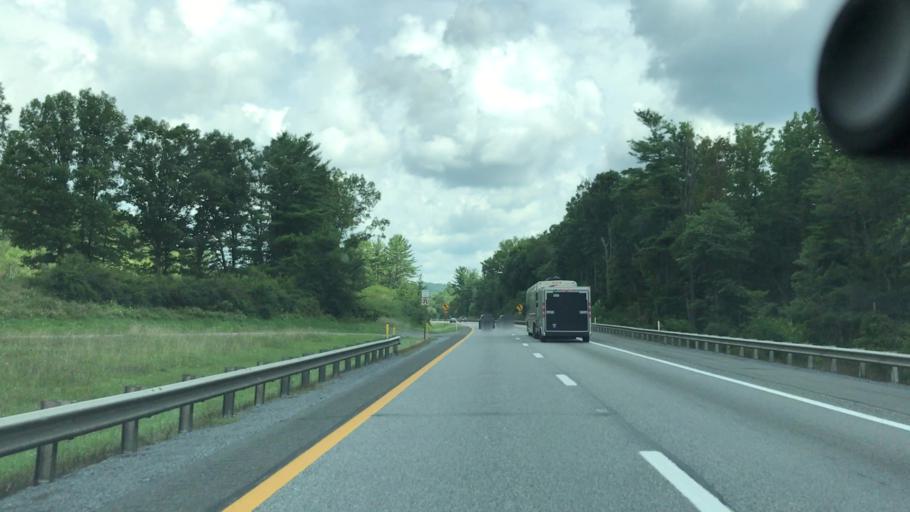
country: US
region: West Virginia
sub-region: Mercer County
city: Athens
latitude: 37.4537
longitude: -81.0645
